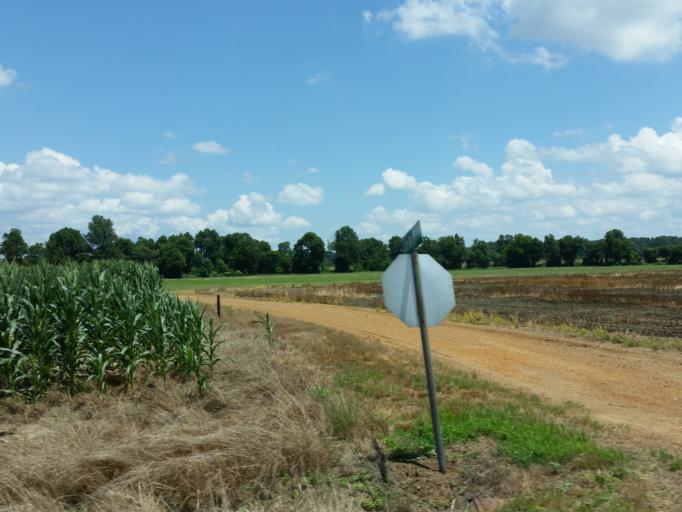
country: US
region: Kentucky
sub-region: Fulton County
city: Hickman
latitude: 36.5575
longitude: -89.2837
